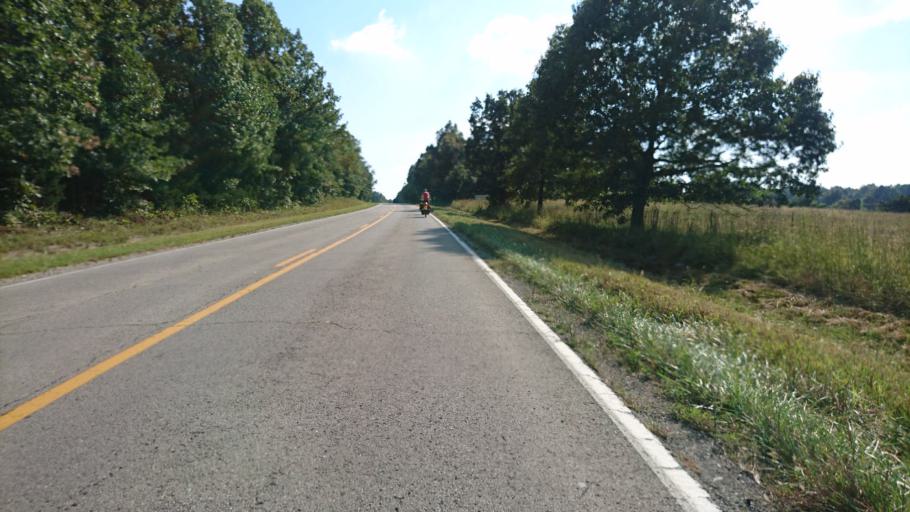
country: US
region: Missouri
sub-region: Laclede County
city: Lebanon
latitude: 37.6215
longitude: -92.6931
